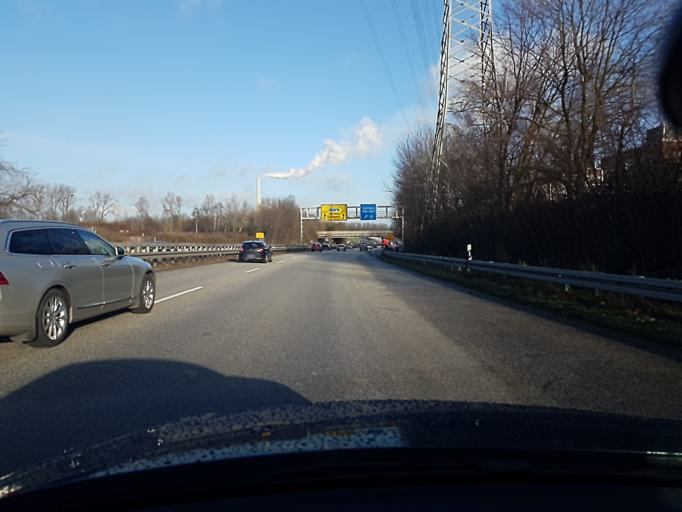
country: DE
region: North Rhine-Westphalia
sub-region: Regierungsbezirk Dusseldorf
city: Essen
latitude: 51.4994
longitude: 6.9958
